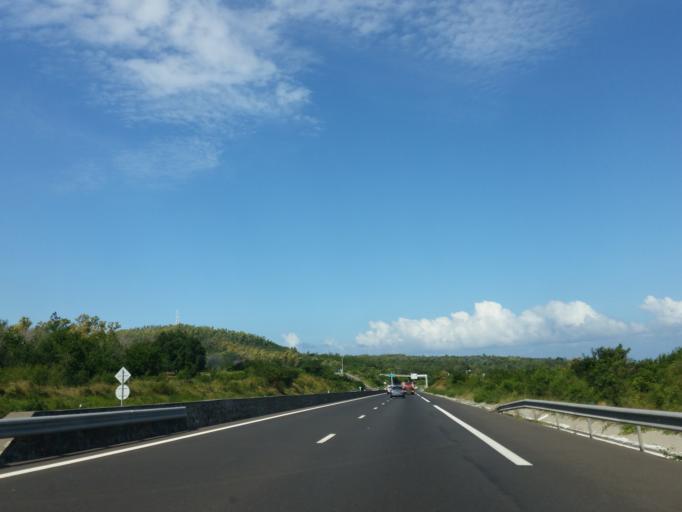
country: RE
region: Reunion
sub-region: Reunion
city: Les Avirons
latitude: -21.2586
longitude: 55.3344
